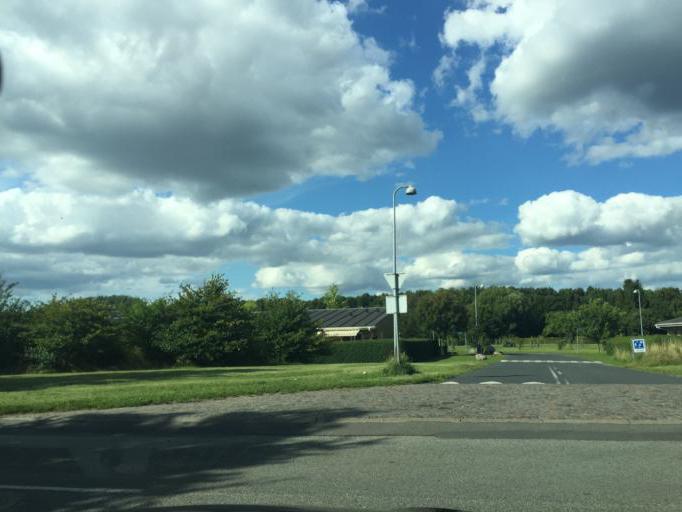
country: DK
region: South Denmark
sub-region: Odense Kommune
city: Odense
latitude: 55.3680
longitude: 10.4067
